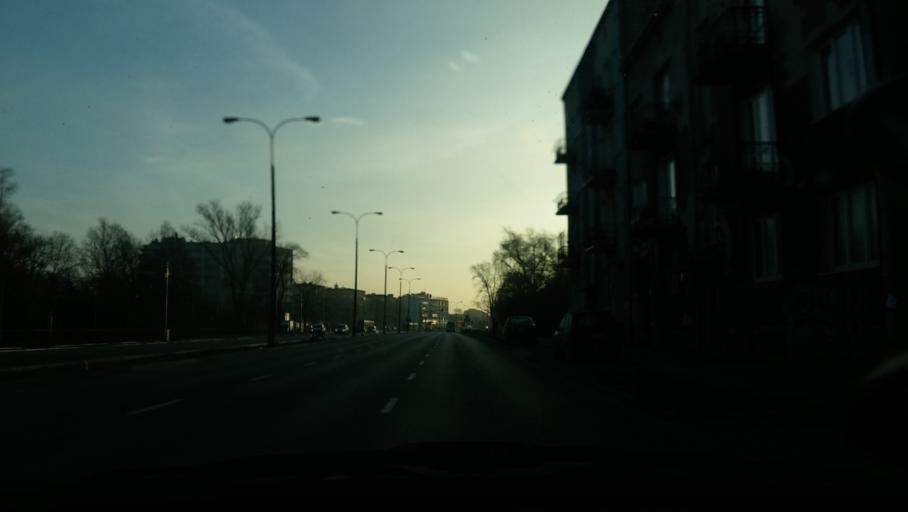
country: PL
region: Masovian Voivodeship
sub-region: Warszawa
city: Praga Poludnie
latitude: 52.2405
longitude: 21.1104
